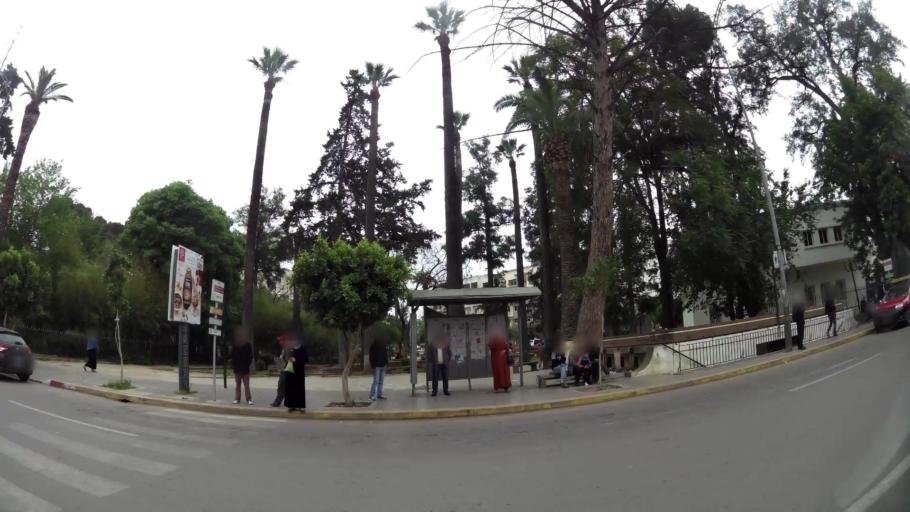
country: MA
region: Fes-Boulemane
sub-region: Fes
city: Fes
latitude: 34.0383
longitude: -4.9977
